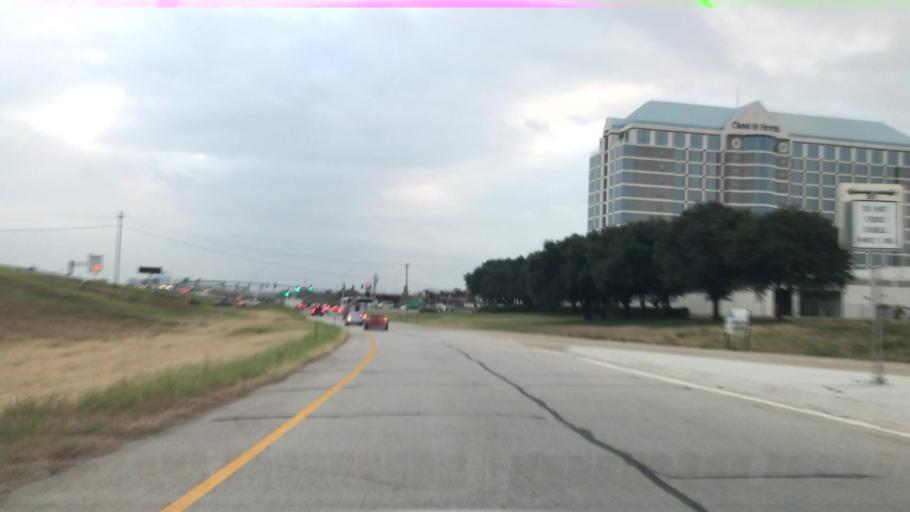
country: US
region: Texas
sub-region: Dallas County
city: Farmers Branch
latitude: 32.9067
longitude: -96.9228
